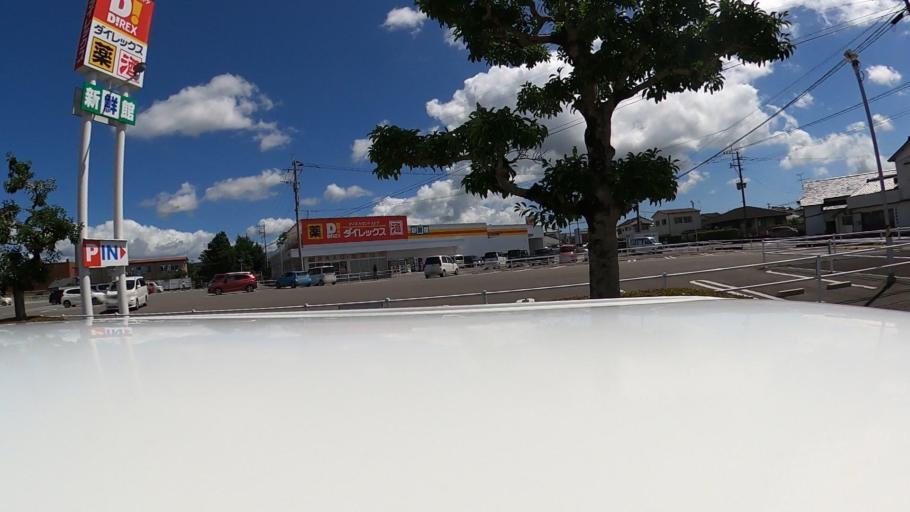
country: JP
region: Miyazaki
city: Tsuma
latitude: 32.1038
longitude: 131.4010
